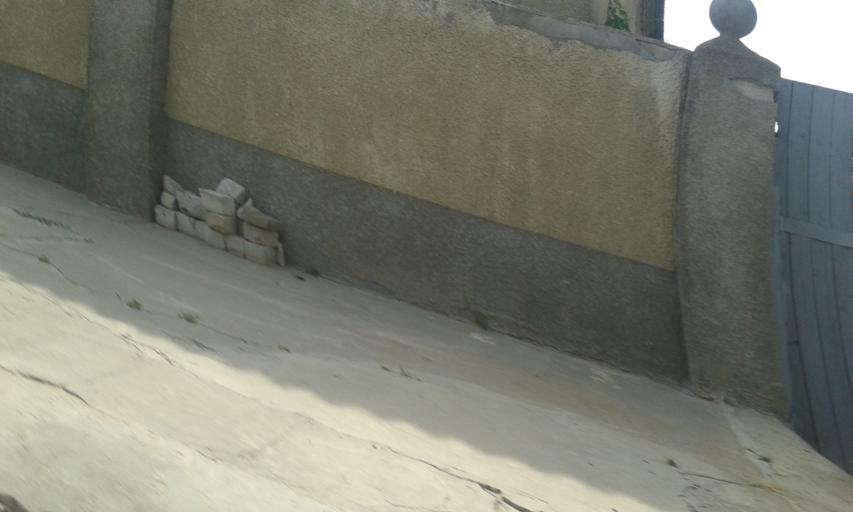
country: RU
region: Volgograd
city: Volgograd
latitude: 48.7596
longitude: 44.4845
